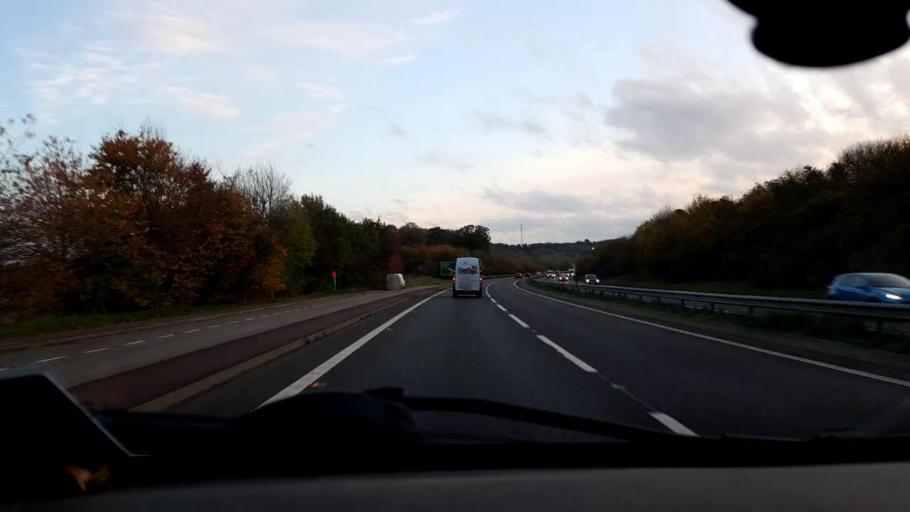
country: GB
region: England
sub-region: Norfolk
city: Bowthorpe
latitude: 52.6373
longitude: 1.1957
